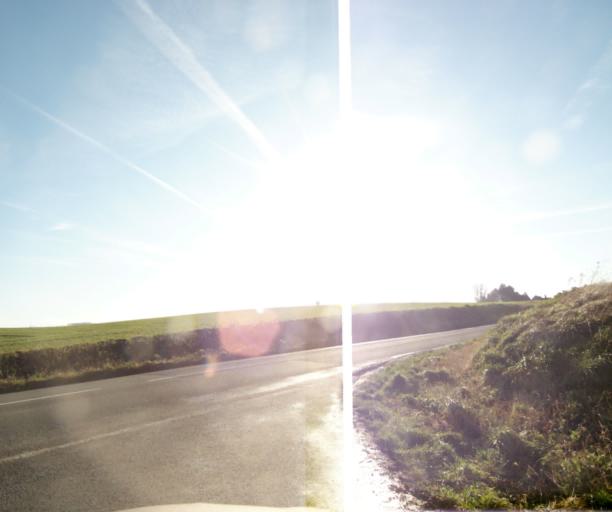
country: FR
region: Nord-Pas-de-Calais
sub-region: Departement du Nord
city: Curgies
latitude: 50.3558
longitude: 3.6047
